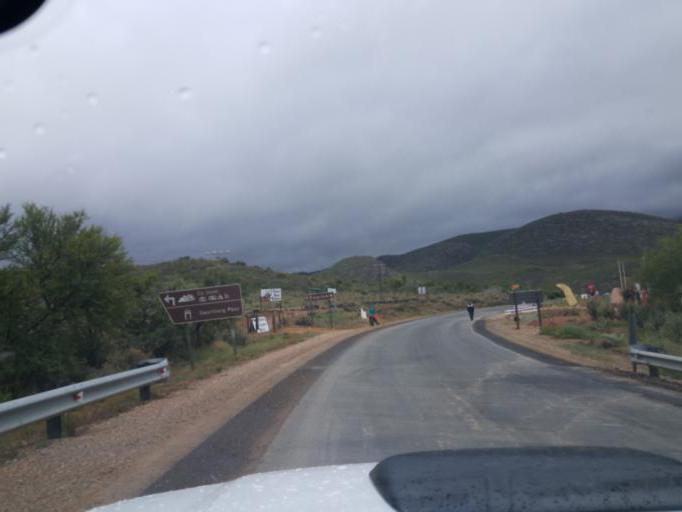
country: ZA
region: Western Cape
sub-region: Eden District Municipality
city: Oudtshoorn
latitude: -33.4042
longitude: 22.2175
